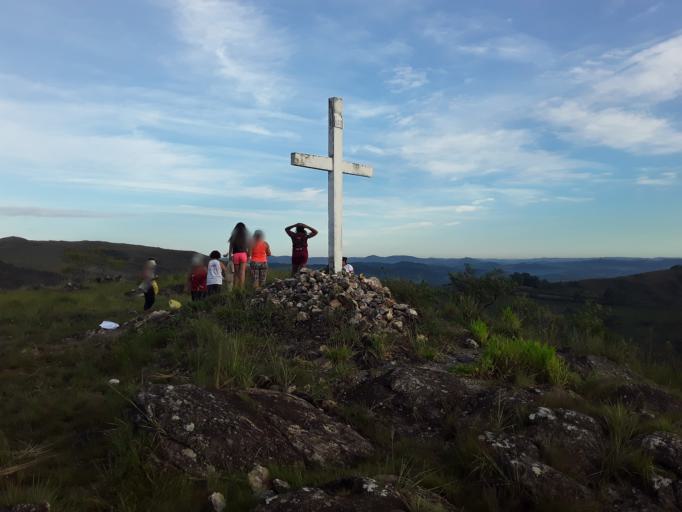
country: BR
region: Minas Gerais
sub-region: Sao Joao Del Rei
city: Sao Joao del Rei
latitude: -21.1298
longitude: -44.2749
